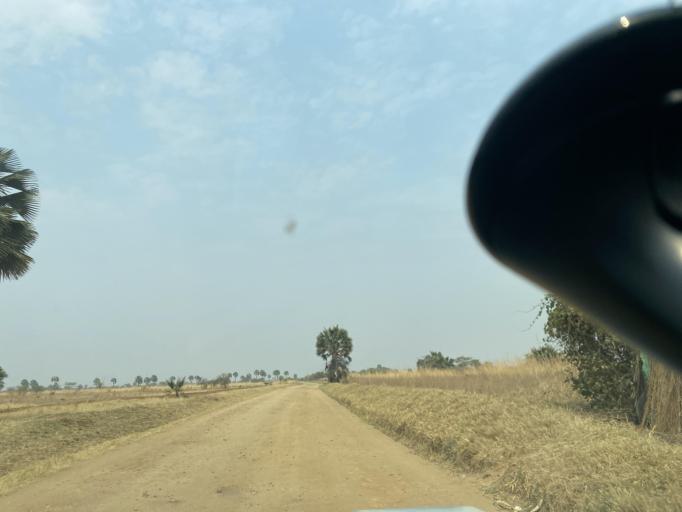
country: ZM
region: Lusaka
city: Kafue
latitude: -15.6481
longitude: 28.0704
